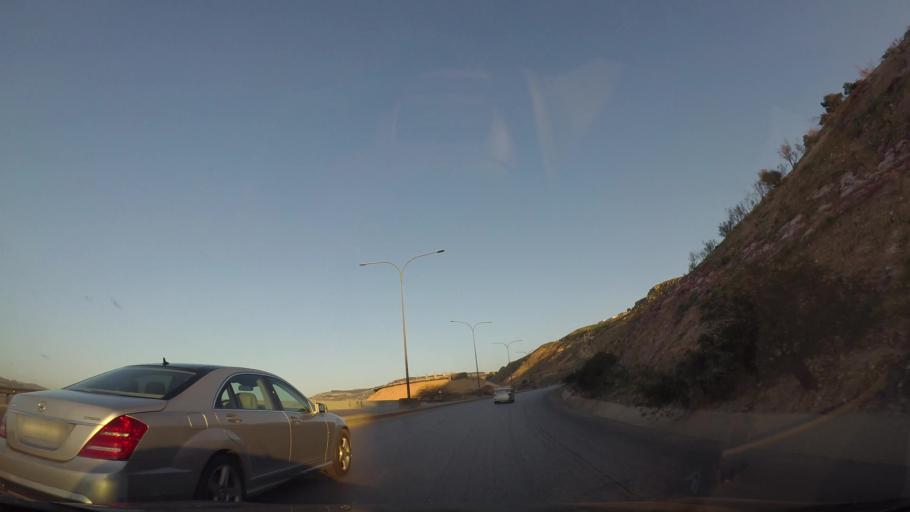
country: JO
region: Balqa
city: Yarqa
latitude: 31.8695
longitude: 35.7349
